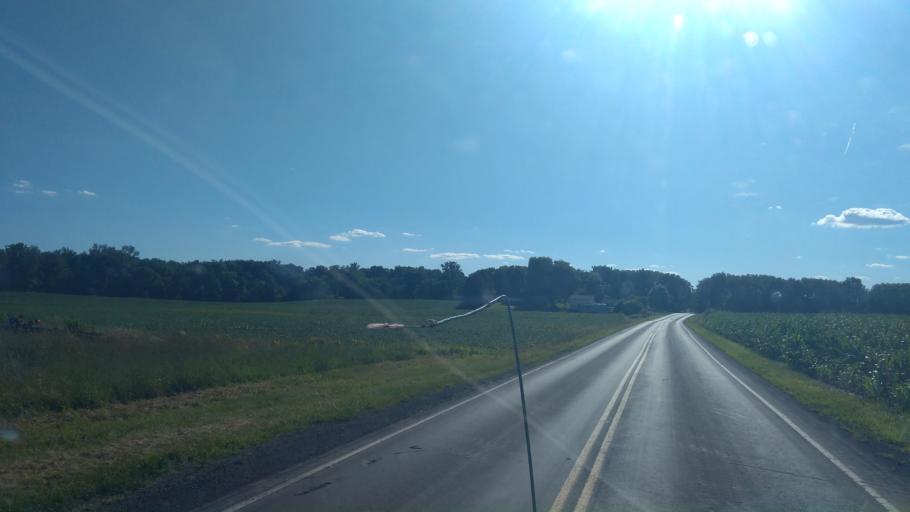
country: US
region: New York
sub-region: Wayne County
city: Clyde
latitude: 43.0011
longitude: -76.8926
